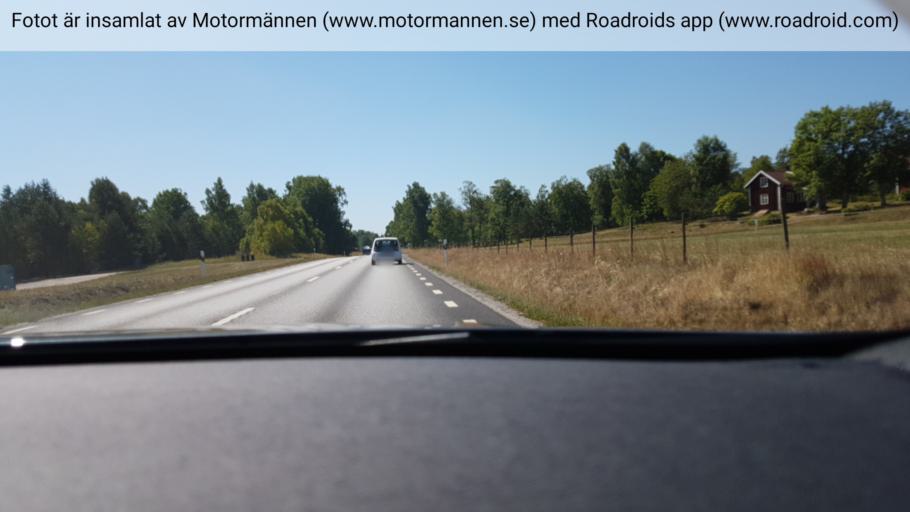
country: SE
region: Joenkoeping
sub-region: Gnosjo Kommun
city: Gnosjoe
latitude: 57.5418
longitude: 13.6898
